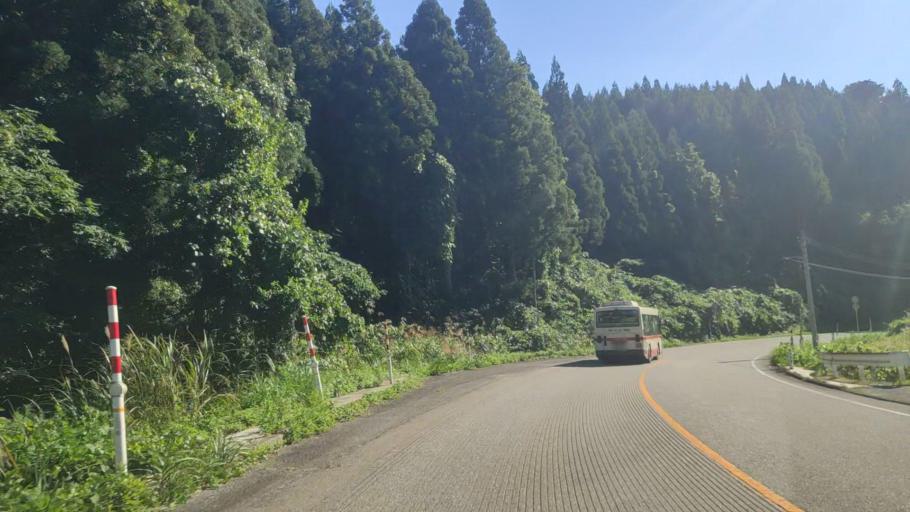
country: JP
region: Ishikawa
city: Nanao
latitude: 37.2423
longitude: 136.9880
